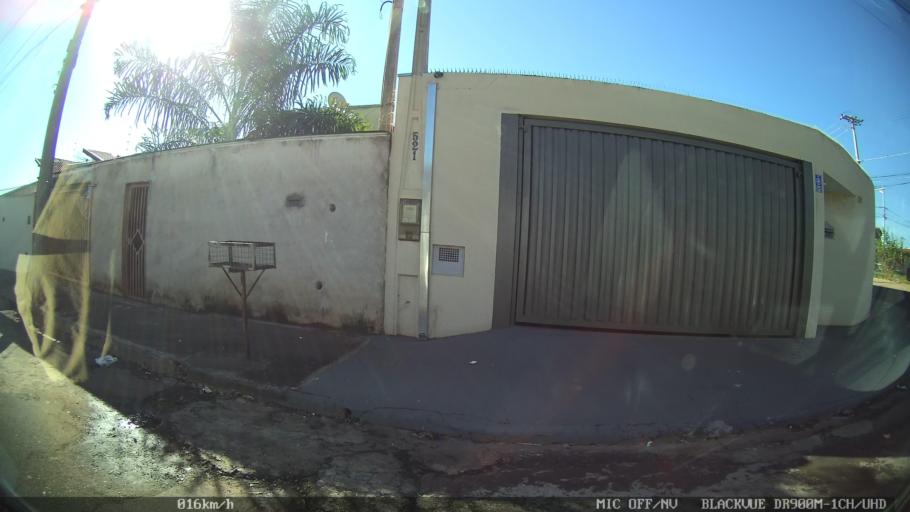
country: BR
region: Sao Paulo
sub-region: Olimpia
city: Olimpia
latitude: -20.7400
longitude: -48.8977
